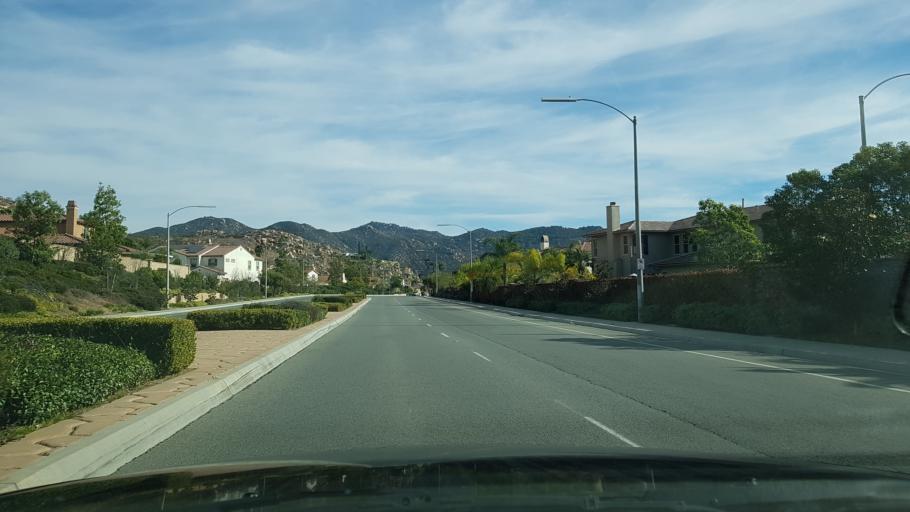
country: US
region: California
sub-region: San Diego County
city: Escondido
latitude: 33.1499
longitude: -117.0470
